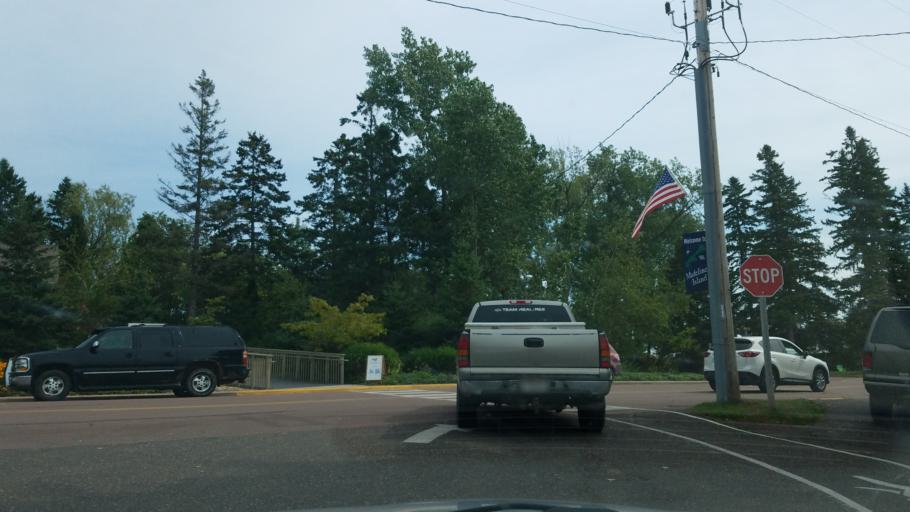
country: US
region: Wisconsin
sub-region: Bayfield County
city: Washburn
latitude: 46.7797
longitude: -90.7886
